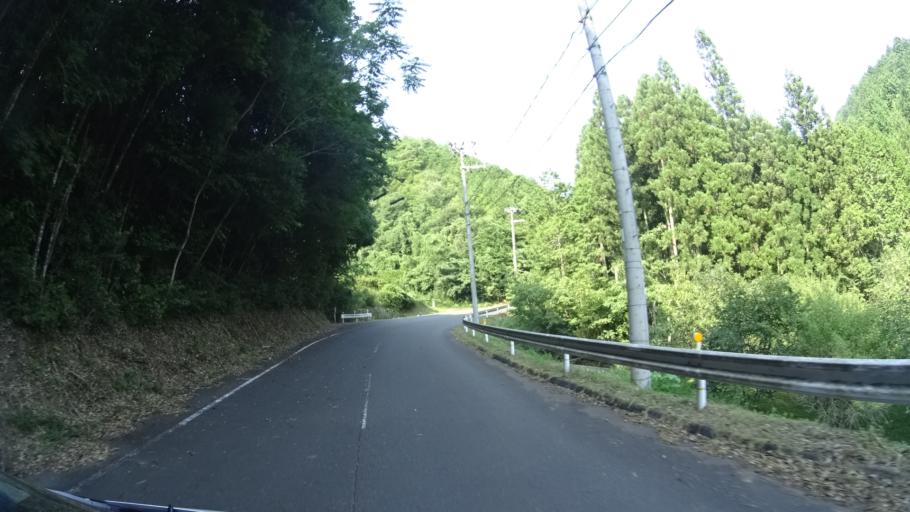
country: JP
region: Kyoto
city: Maizuru
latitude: 35.4347
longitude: 135.2792
